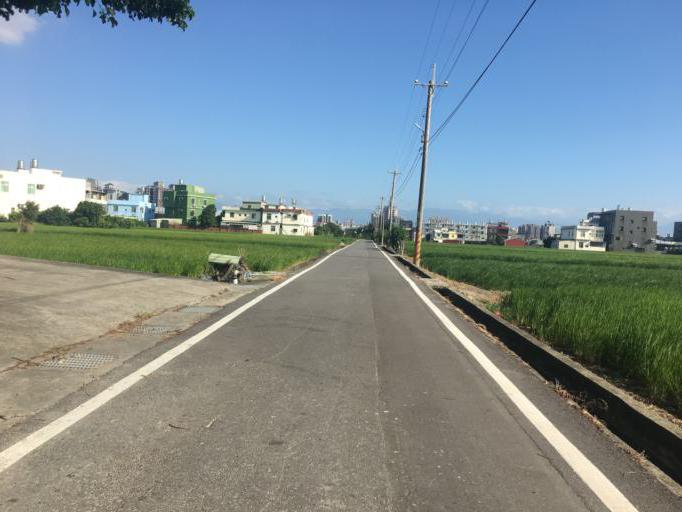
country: TW
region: Taiwan
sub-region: Hsinchu
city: Zhubei
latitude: 24.8388
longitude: 120.9895
